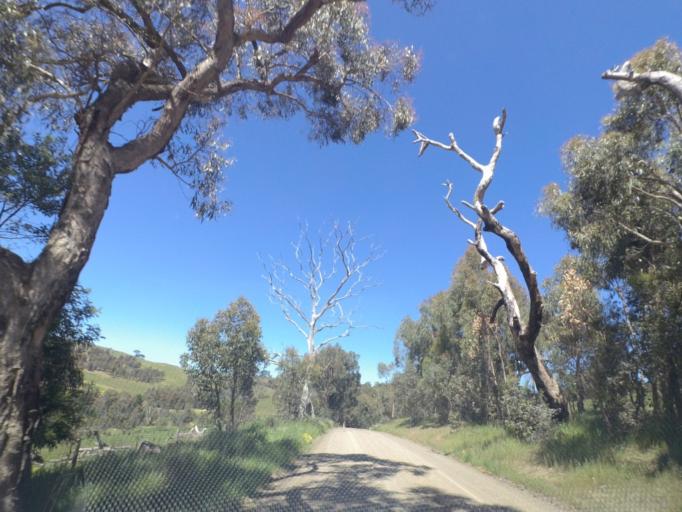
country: AU
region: Victoria
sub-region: Whittlesea
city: Whittlesea
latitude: -37.2770
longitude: 145.0161
